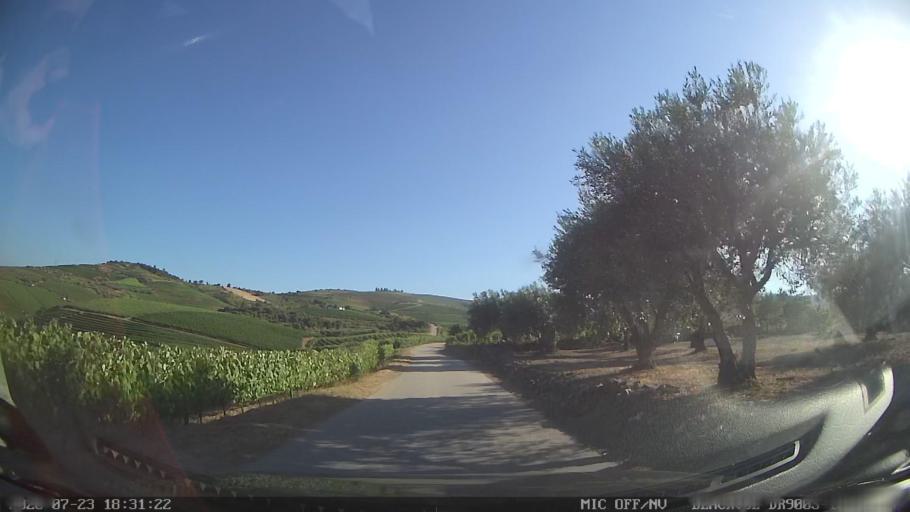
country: PT
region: Viseu
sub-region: Sao Joao da Pesqueira
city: Sao Joao da Pesqueira
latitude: 41.1776
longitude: -7.4055
